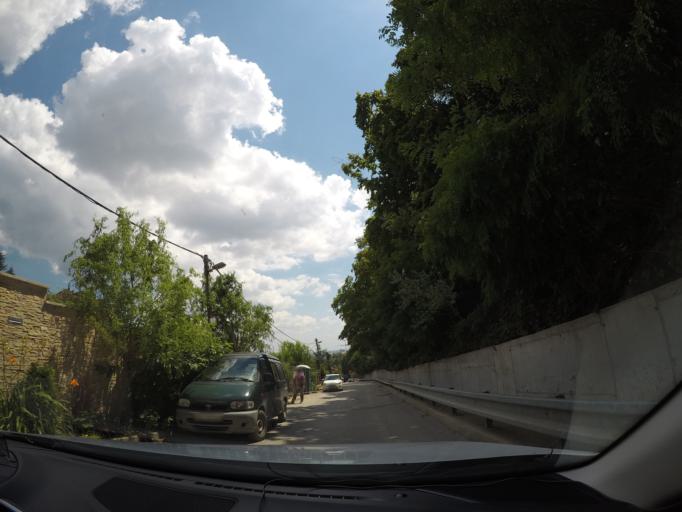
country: SK
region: Bratislavsky
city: Bratislava
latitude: 48.1780
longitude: 17.1118
